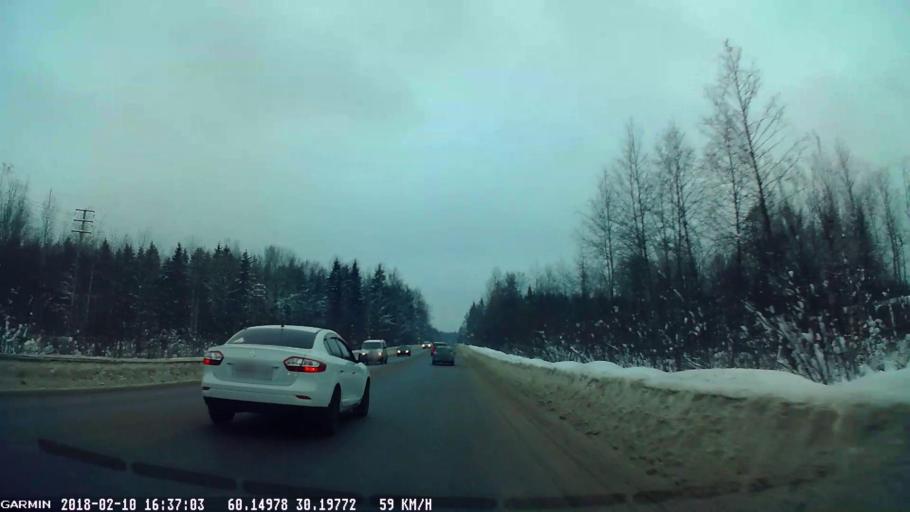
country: RU
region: Leningrad
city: Sertolovo
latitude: 60.1487
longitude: 30.1990
